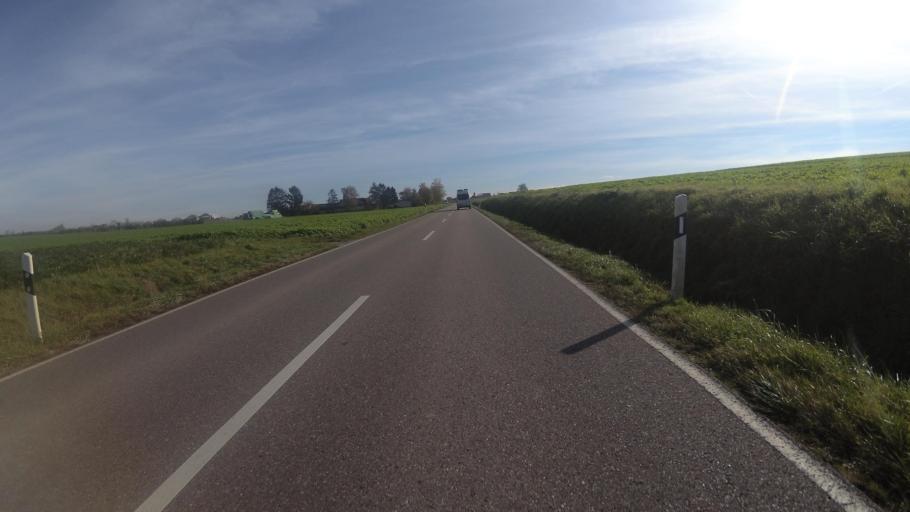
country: DE
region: Baden-Wuerttemberg
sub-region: Regierungsbezirk Stuttgart
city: Gundelsheim
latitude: 49.2667
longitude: 9.1943
